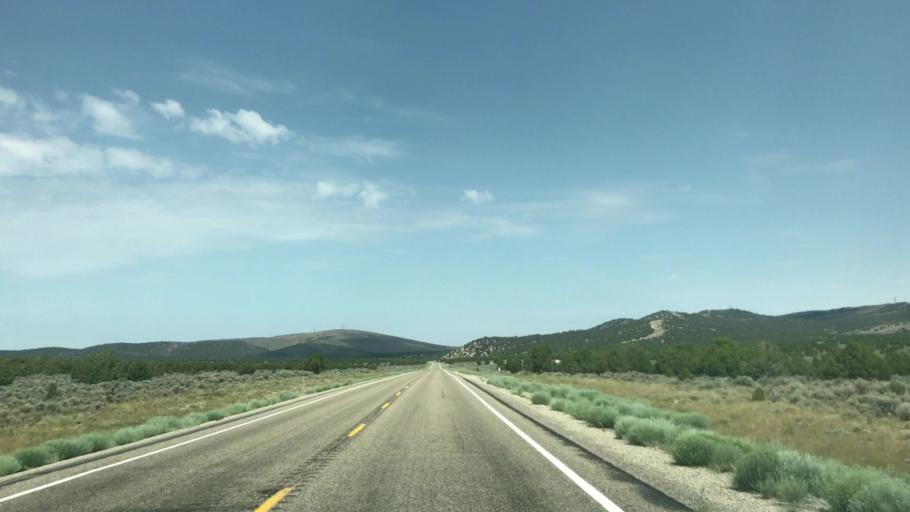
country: US
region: Nevada
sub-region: White Pine County
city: Ely
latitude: 39.3705
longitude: -115.0569
